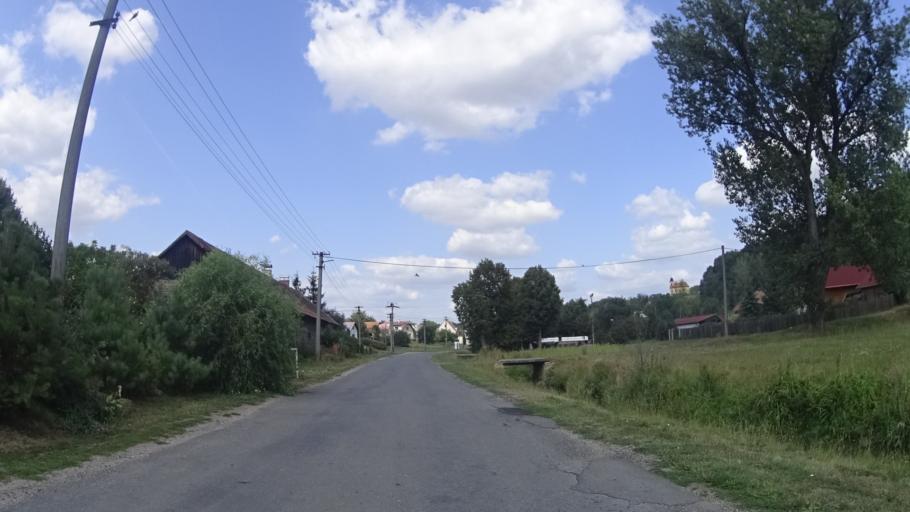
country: CZ
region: Kralovehradecky
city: Kopidlno
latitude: 50.3851
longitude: 15.2978
